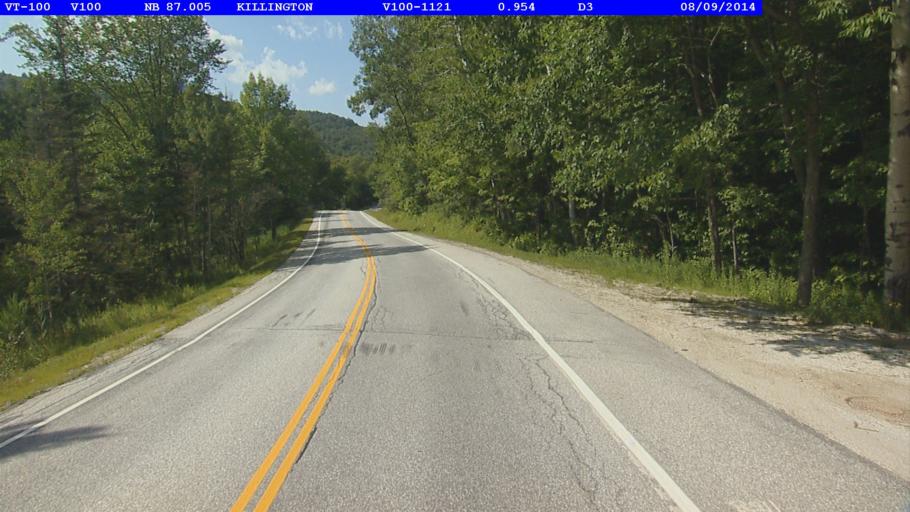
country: US
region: Vermont
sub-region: Rutland County
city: Rutland
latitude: 43.6803
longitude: -72.8111
